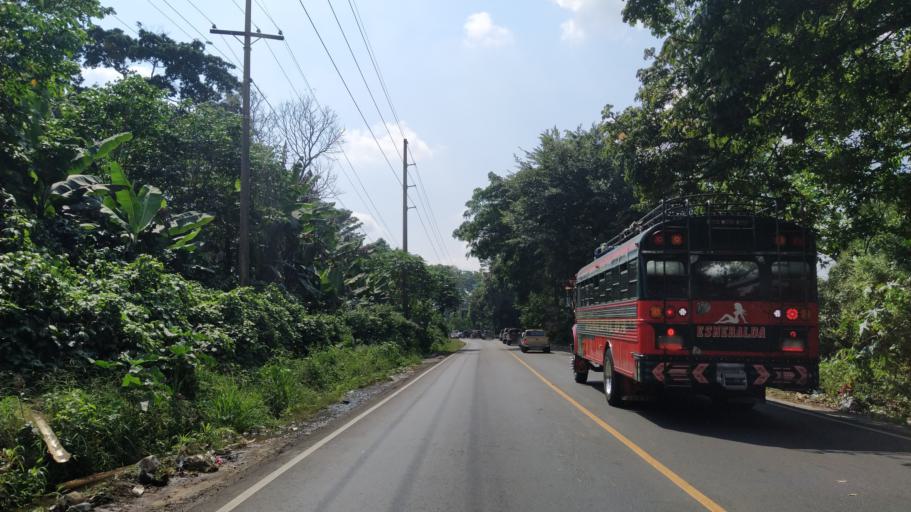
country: GT
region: Quetzaltenango
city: El Palmar
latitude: 14.6389
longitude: -91.5757
